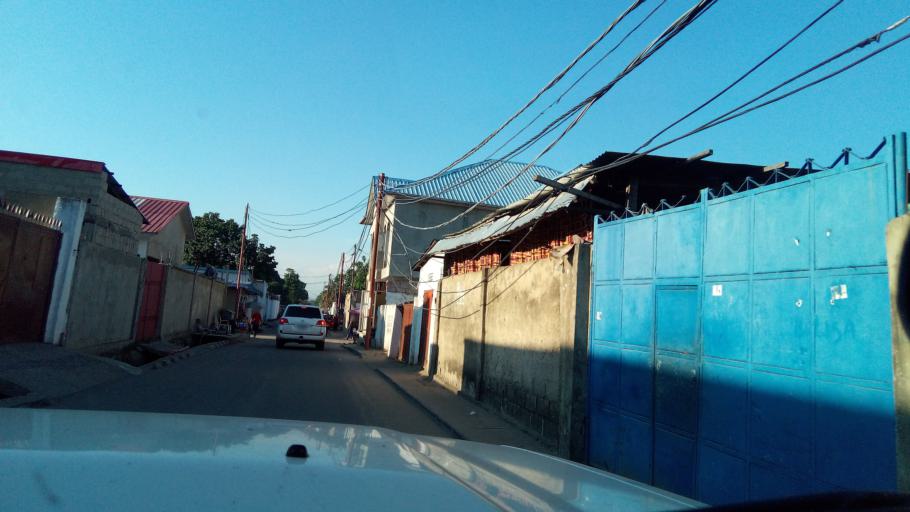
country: CD
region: Kinshasa
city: Kinshasa
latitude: -4.3433
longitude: 15.2683
